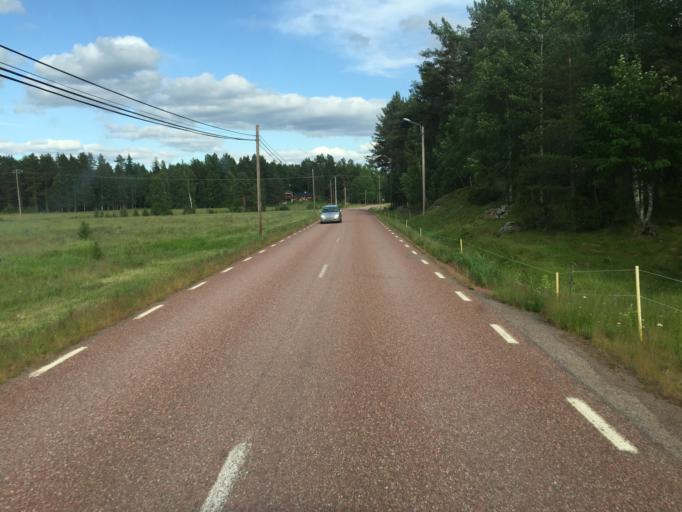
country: SE
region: Dalarna
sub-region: Alvdalens Kommun
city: AElvdalen
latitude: 60.9548
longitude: 13.9252
